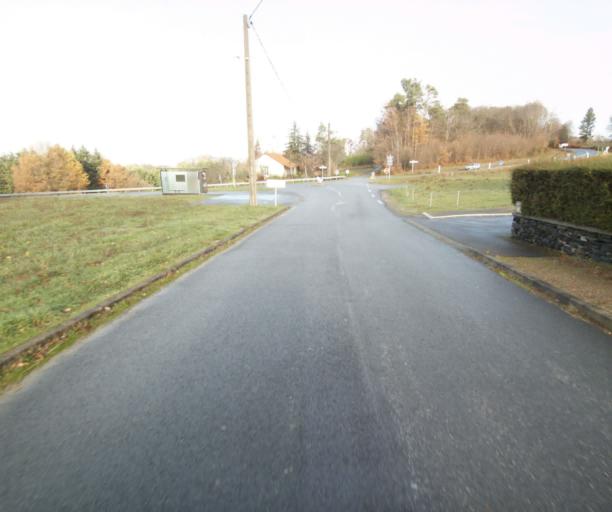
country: FR
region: Limousin
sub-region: Departement de la Correze
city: Saint-Mexant
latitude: 45.2452
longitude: 1.6282
